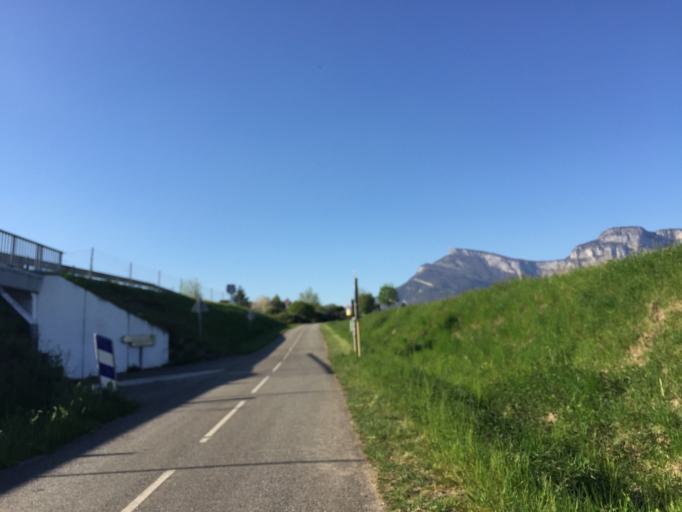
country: FR
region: Rhone-Alpes
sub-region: Departement de la Savoie
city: Saint-Baldoph
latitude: 45.5365
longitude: 5.9689
